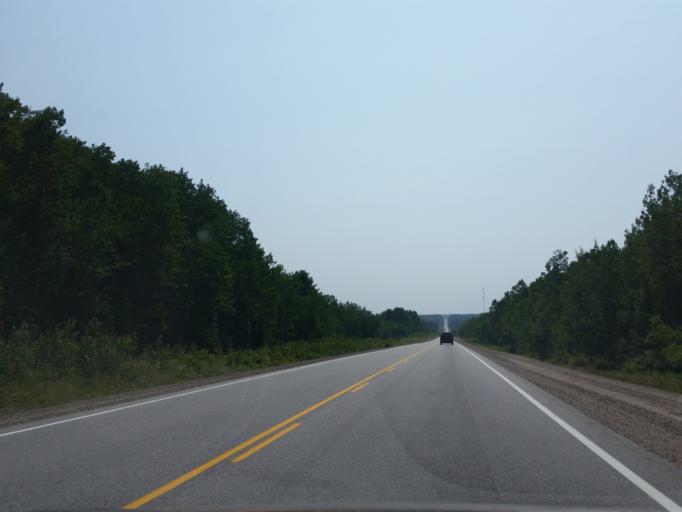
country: CA
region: Ontario
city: Mattawa
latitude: 46.2976
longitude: -78.5509
